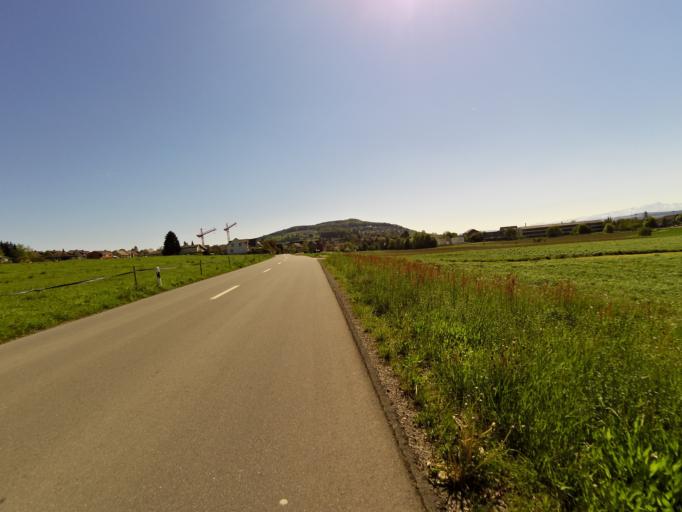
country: CH
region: Thurgau
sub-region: Weinfelden District
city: Maerstetten-Dorf
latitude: 47.5930
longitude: 9.0606
